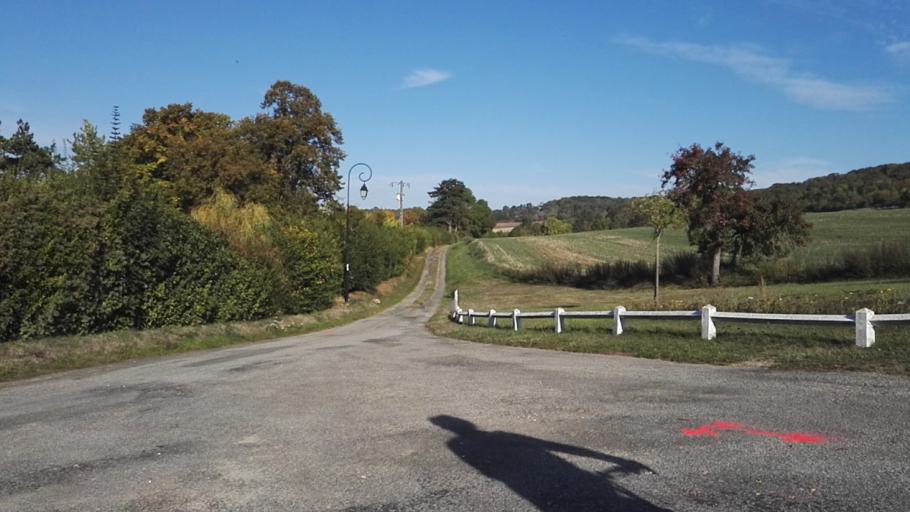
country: FR
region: Haute-Normandie
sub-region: Departement de l'Eure
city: Menilles
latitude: 49.0526
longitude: 1.3398
